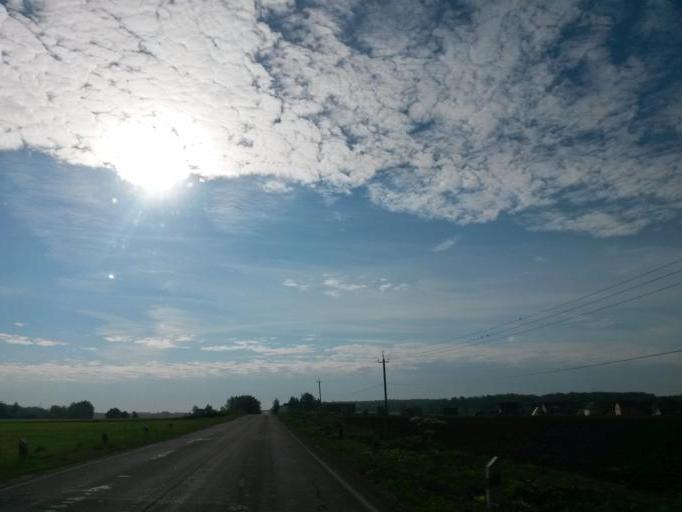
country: RU
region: Moskovskaya
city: Belyye Stolby
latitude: 55.2682
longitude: 37.7746
